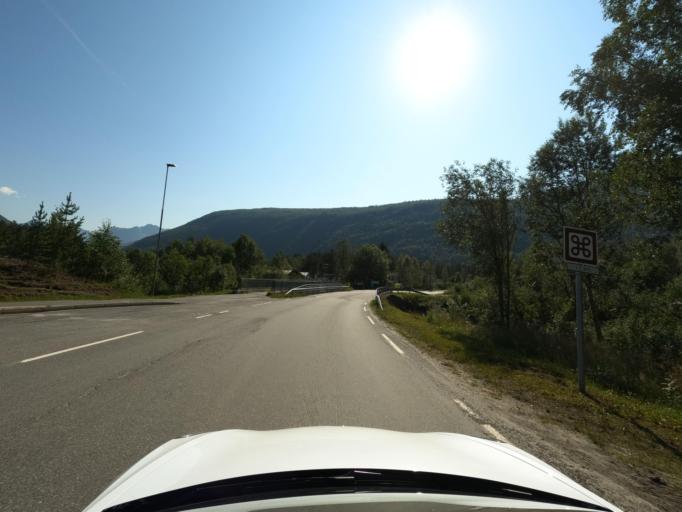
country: NO
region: Nordland
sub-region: Narvik
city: Bjerkvik
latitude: 68.3720
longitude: 17.6031
